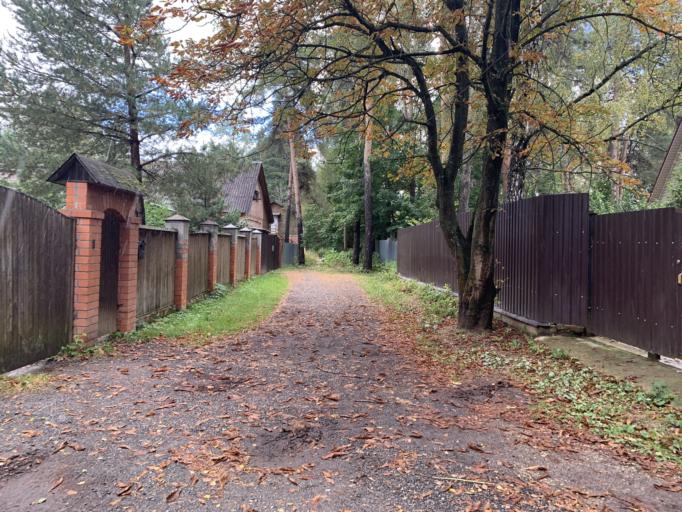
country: RU
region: Moskovskaya
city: Mamontovka
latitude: 55.9851
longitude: 37.8275
